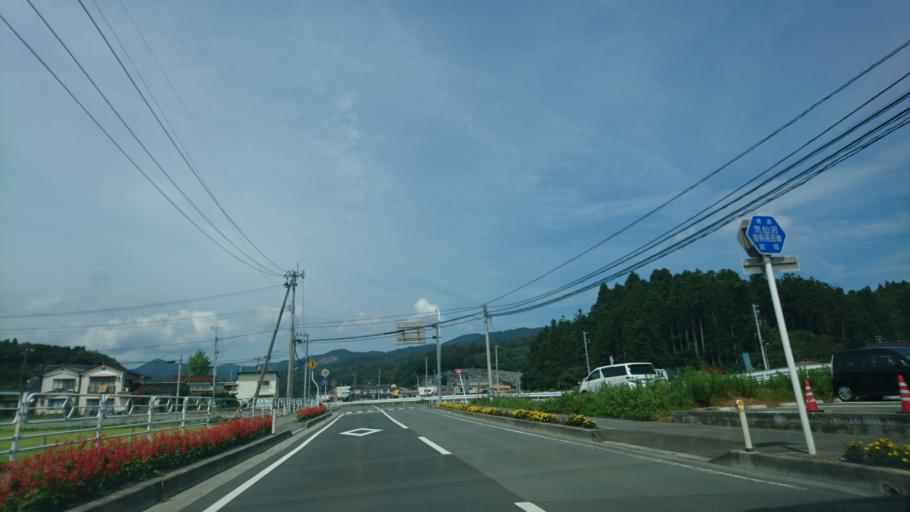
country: JP
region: Iwate
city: Ofunato
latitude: 38.9229
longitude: 141.5830
